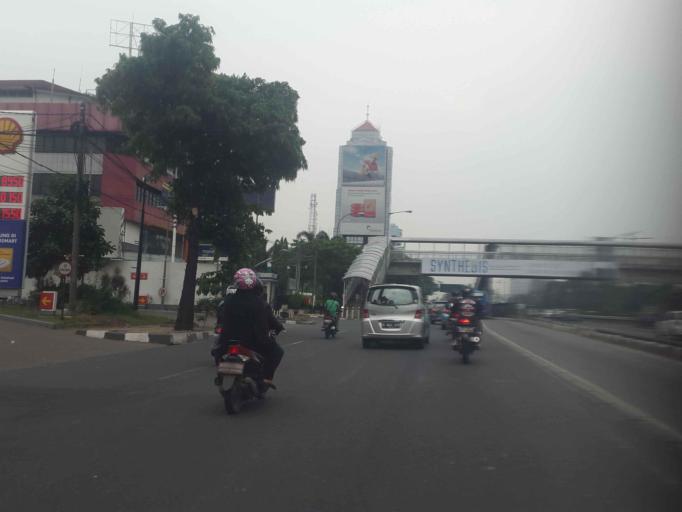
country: ID
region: Jakarta Raya
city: Jakarta
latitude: -6.2412
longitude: 106.8367
